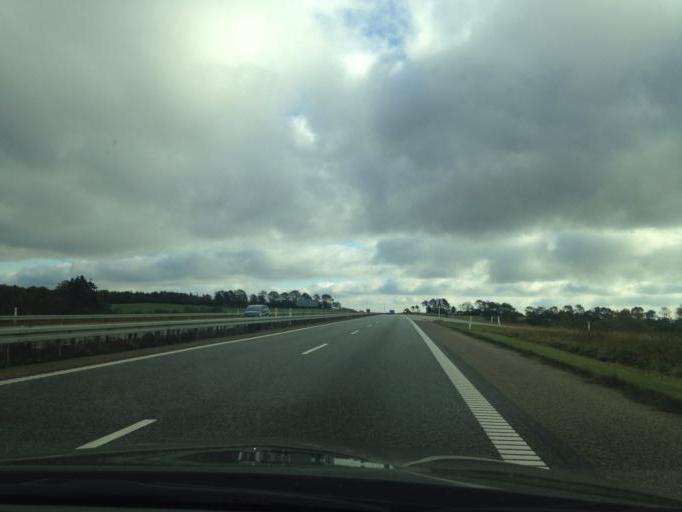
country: DK
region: South Denmark
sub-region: Vejle Kommune
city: Give
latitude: 55.8348
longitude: 9.3128
